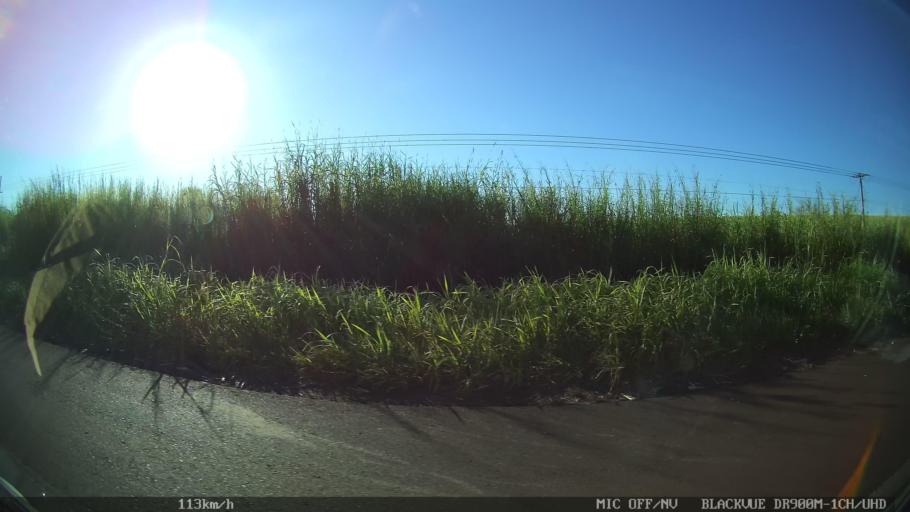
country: BR
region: Sao Paulo
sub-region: Olimpia
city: Olimpia
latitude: -20.7302
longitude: -49.0543
